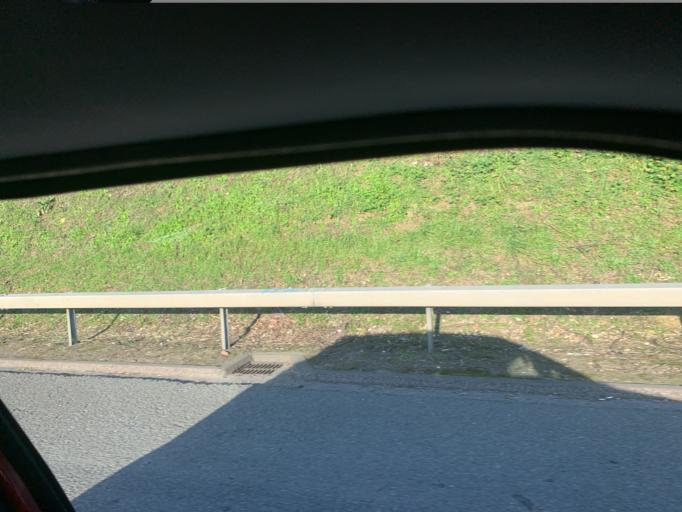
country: GB
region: England
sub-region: Surrey
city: Leatherhead
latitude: 51.3018
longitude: -0.3188
